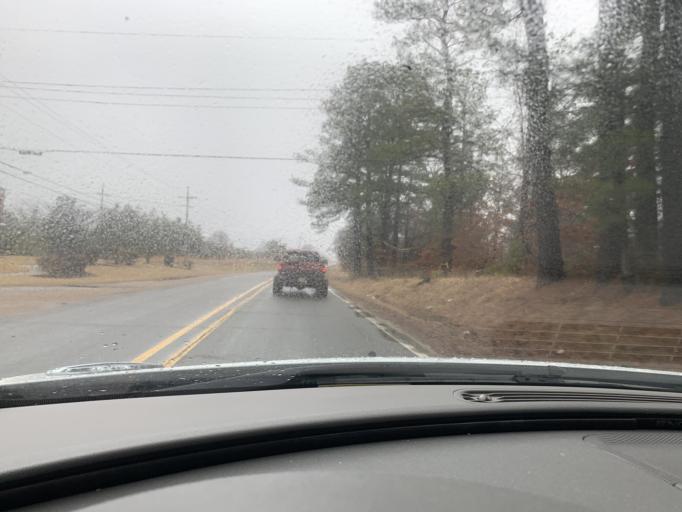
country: US
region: Mississippi
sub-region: De Soto County
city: Horn Lake
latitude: 34.9246
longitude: -90.0097
